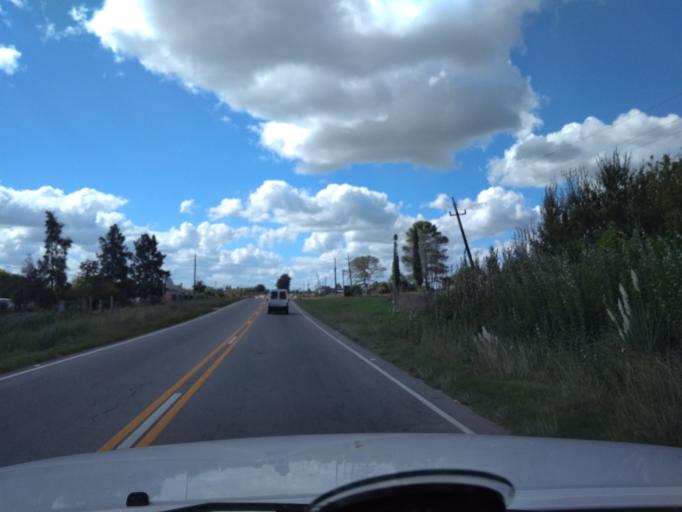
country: UY
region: Canelones
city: Joaquin Suarez
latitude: -34.6933
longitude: -56.0553
